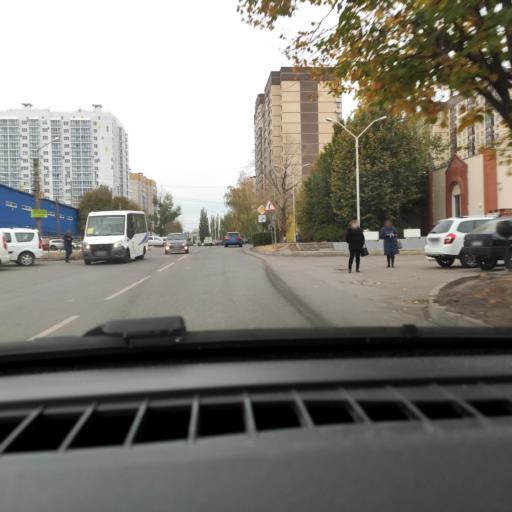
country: RU
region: Voronezj
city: Podgornoye
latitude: 51.6936
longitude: 39.1350
